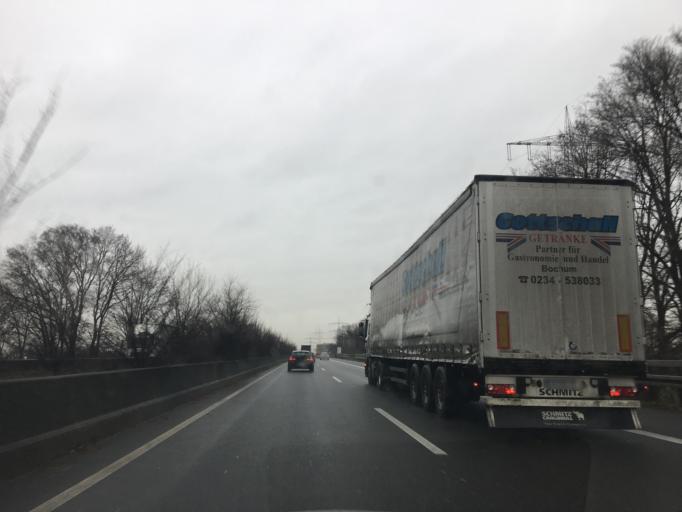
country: DE
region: North Rhine-Westphalia
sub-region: Regierungsbezirk Dusseldorf
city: Dormagen
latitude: 51.1068
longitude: 6.8002
